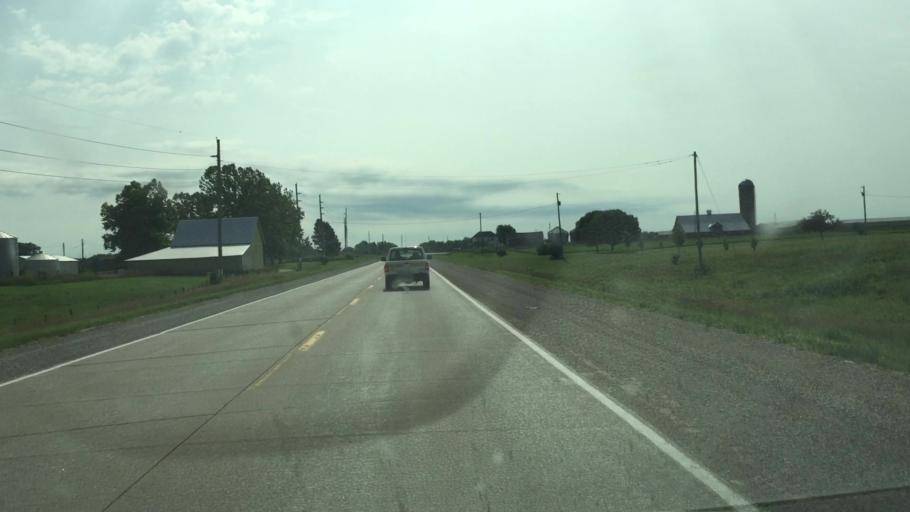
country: US
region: Illinois
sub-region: Hancock County
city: Nauvoo
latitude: 40.6319
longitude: -91.5055
